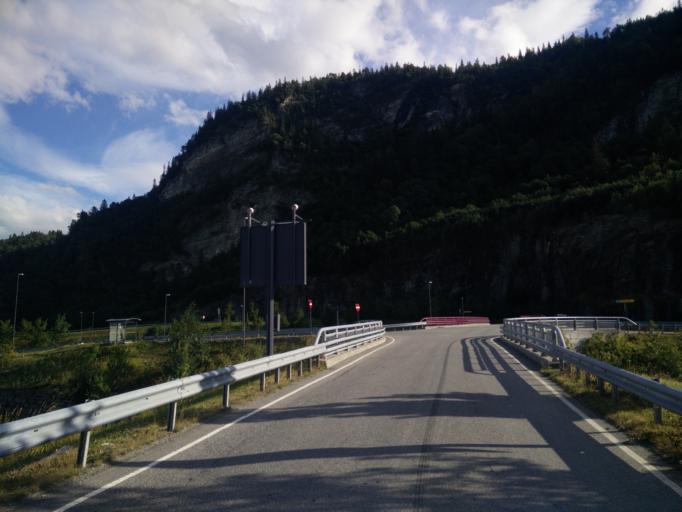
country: NO
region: Sor-Trondelag
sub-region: Melhus
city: Melhus
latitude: 63.3245
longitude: 10.2154
